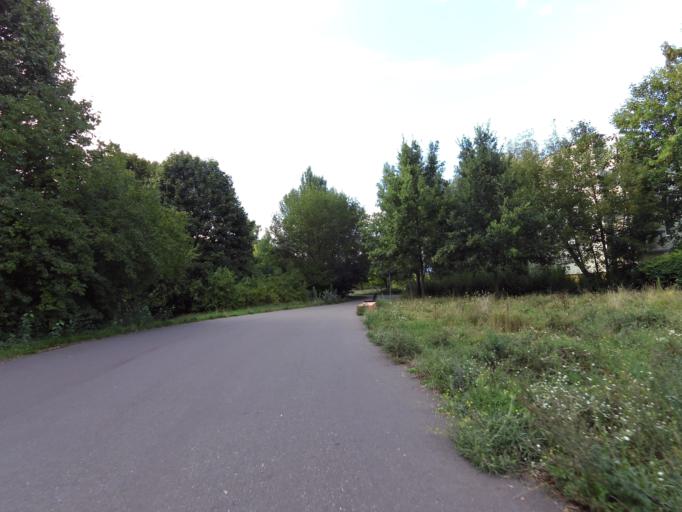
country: DE
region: Berlin
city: Baumschulenweg
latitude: 52.4691
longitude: 13.4743
